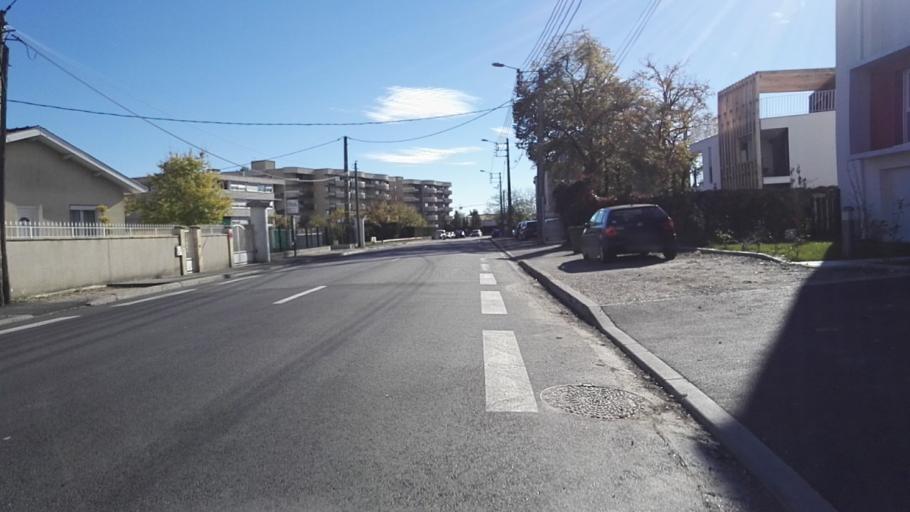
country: FR
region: Aquitaine
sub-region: Departement de la Gironde
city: Merignac
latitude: 44.8491
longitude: -0.6440
